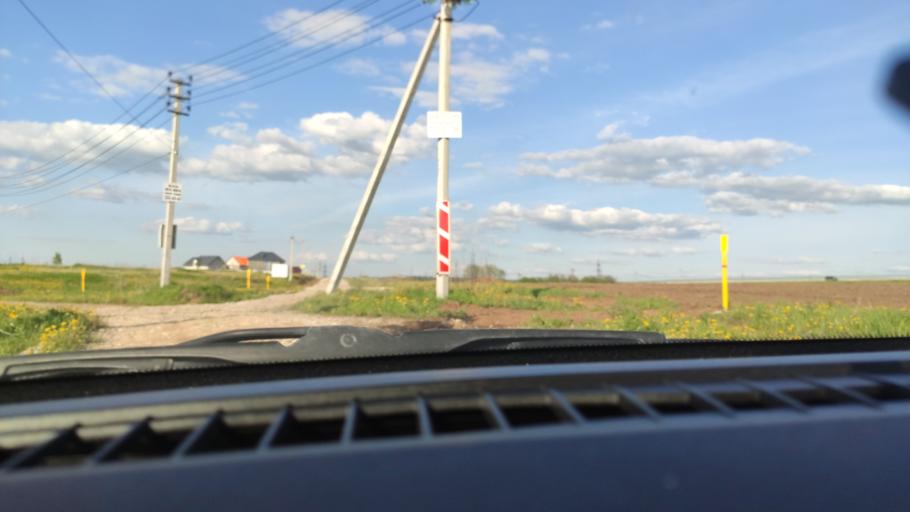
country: RU
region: Perm
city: Ferma
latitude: 57.9355
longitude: 56.3519
